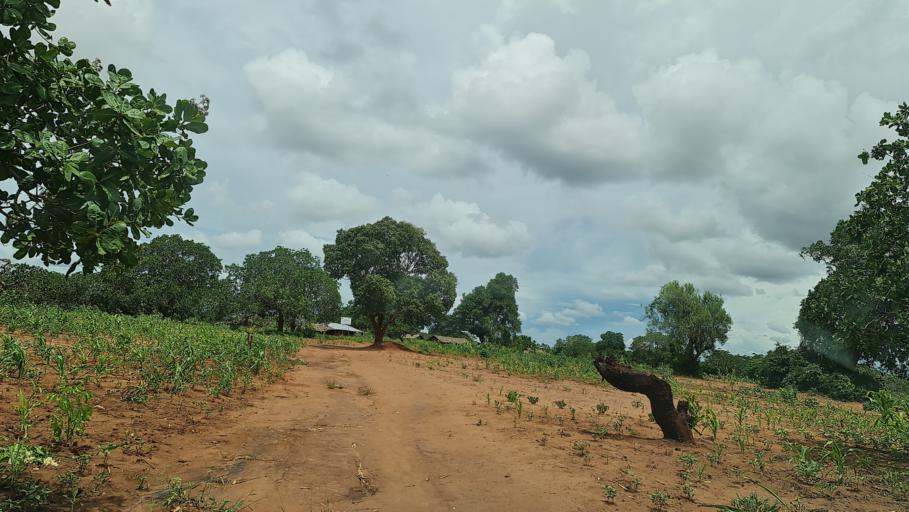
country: MZ
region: Nampula
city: Nacala
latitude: -14.7787
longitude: 39.9952
